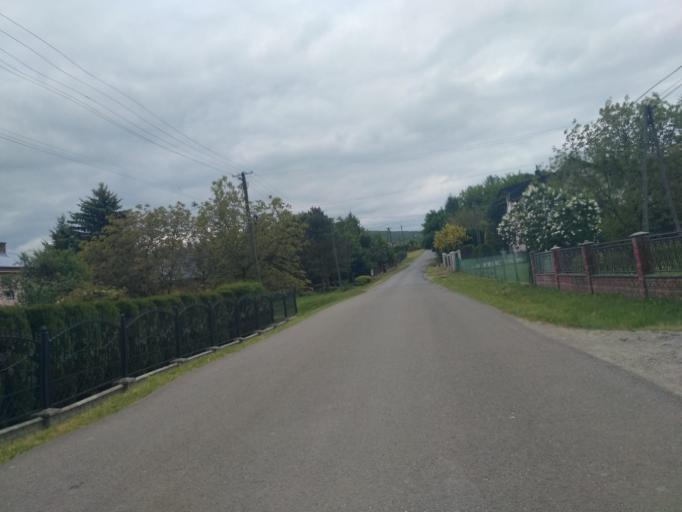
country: PL
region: Subcarpathian Voivodeship
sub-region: Powiat krosnienski
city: Jedlicze
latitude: 49.6957
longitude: 21.6396
